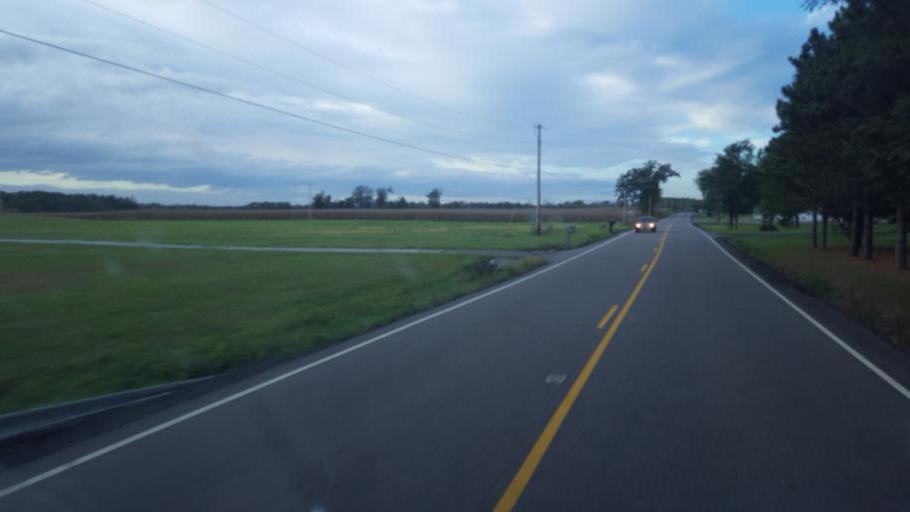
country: US
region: Ohio
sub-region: Licking County
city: Utica
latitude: 40.2651
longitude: -82.5169
